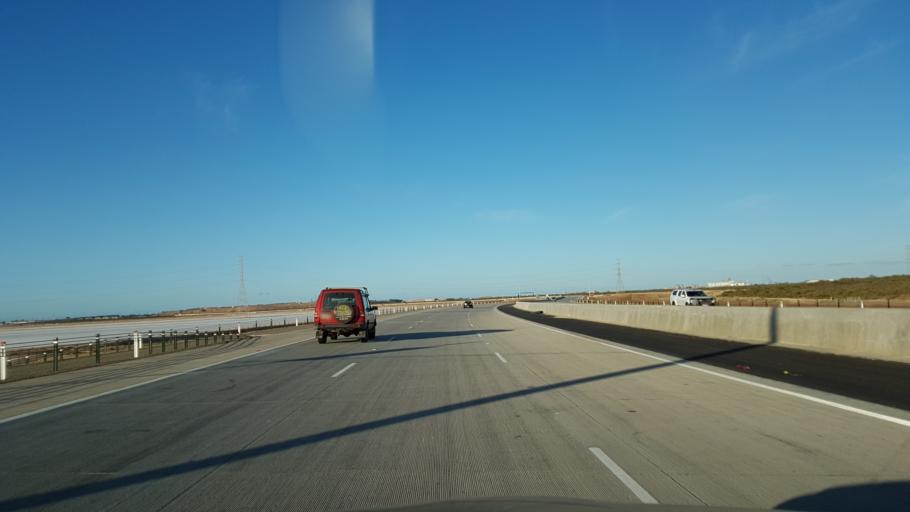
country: AU
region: South Australia
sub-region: Port Adelaide Enfield
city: Enfield
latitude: -34.8060
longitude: 138.5727
